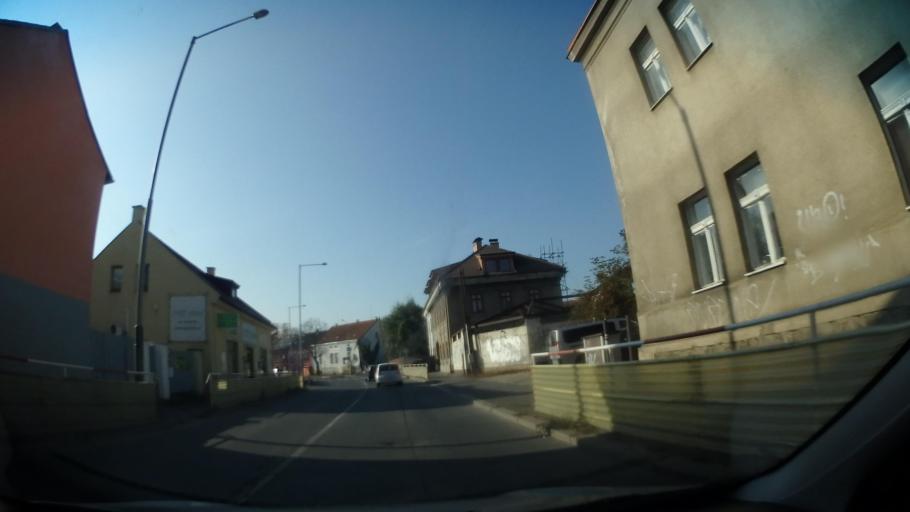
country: CZ
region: Praha
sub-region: Praha 9
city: Vysocany
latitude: 50.0858
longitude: 14.5124
